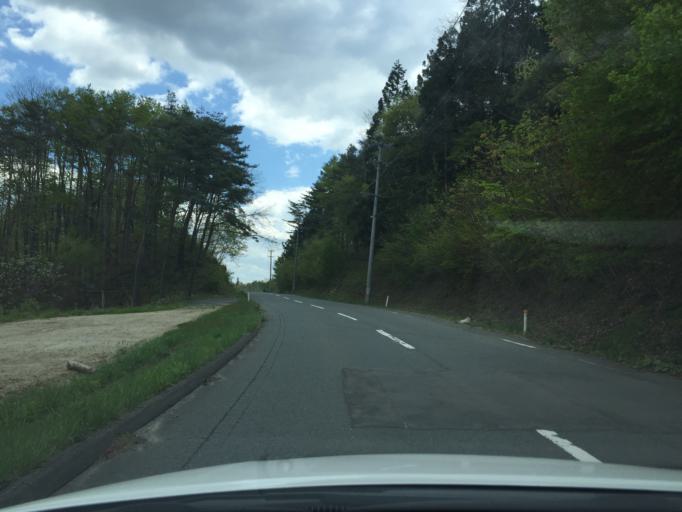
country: JP
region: Fukushima
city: Yanagawamachi-saiwaicho
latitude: 37.6868
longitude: 140.7154
